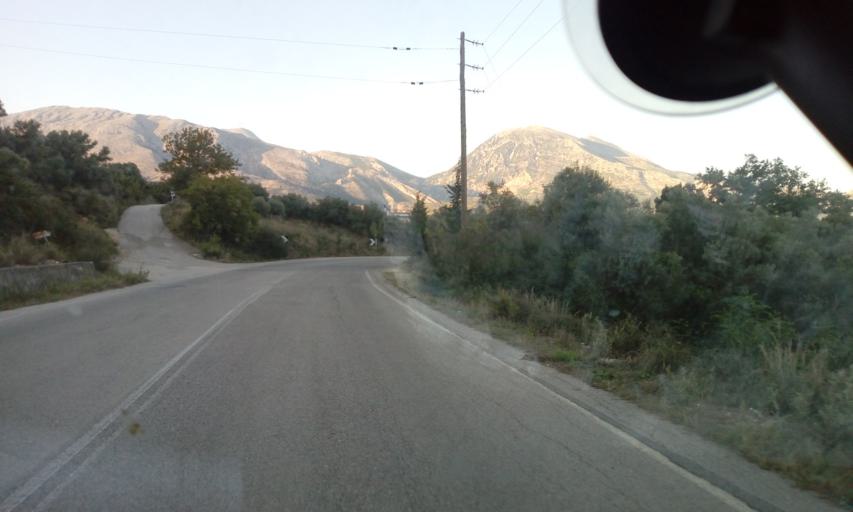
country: GR
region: West Greece
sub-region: Nomos Aitolias kai Akarnanias
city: Kandila
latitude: 38.6777
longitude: 20.9298
